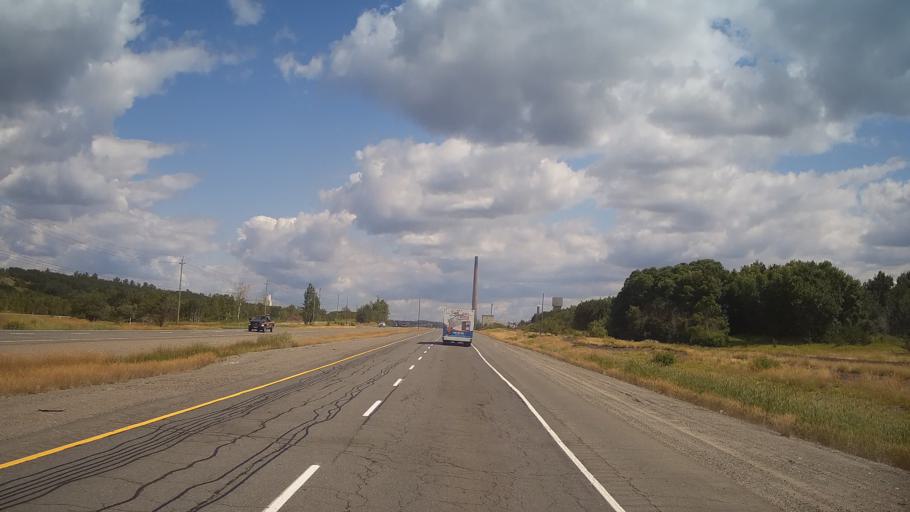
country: CA
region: Ontario
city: Greater Sudbury
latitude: 46.4512
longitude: -81.0926
